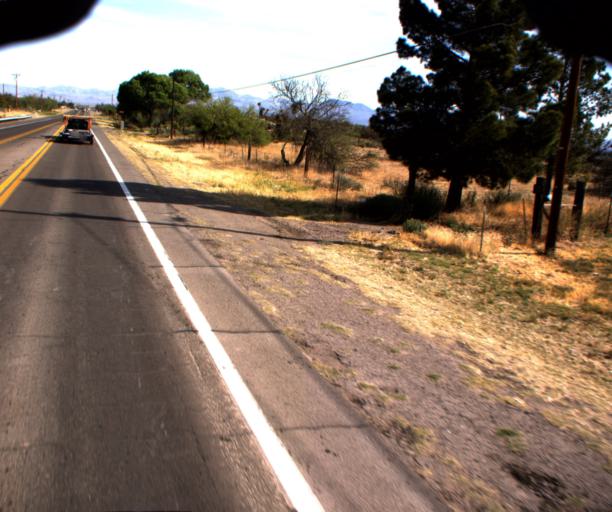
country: US
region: Arizona
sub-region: Graham County
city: Cactus Flat
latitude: 32.7600
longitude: -109.7163
